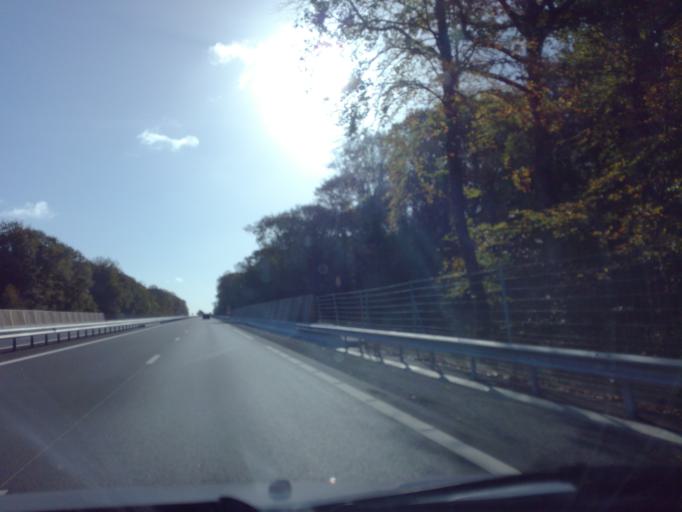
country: FR
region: Pays de la Loire
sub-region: Departement de la Loire-Atlantique
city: Soudan
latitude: 47.7837
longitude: -1.2525
